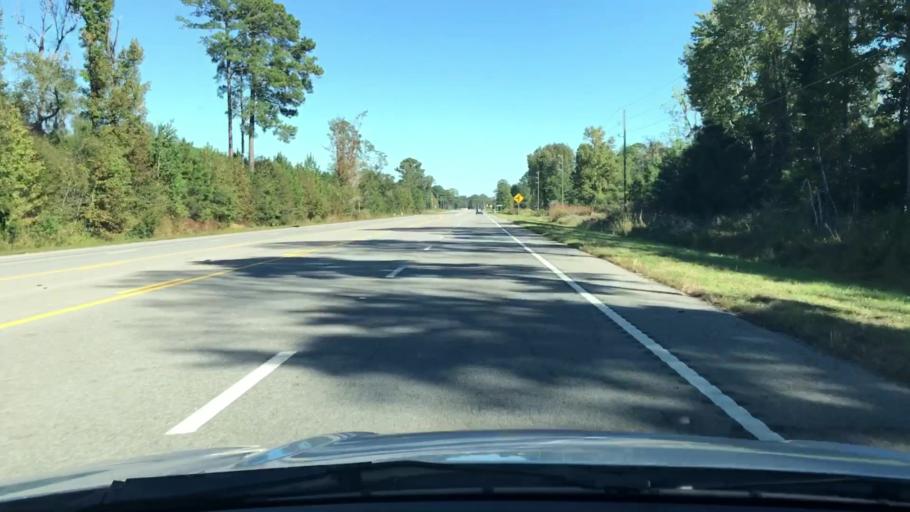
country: US
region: South Carolina
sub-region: Charleston County
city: Ravenel
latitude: 32.7718
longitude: -80.4729
